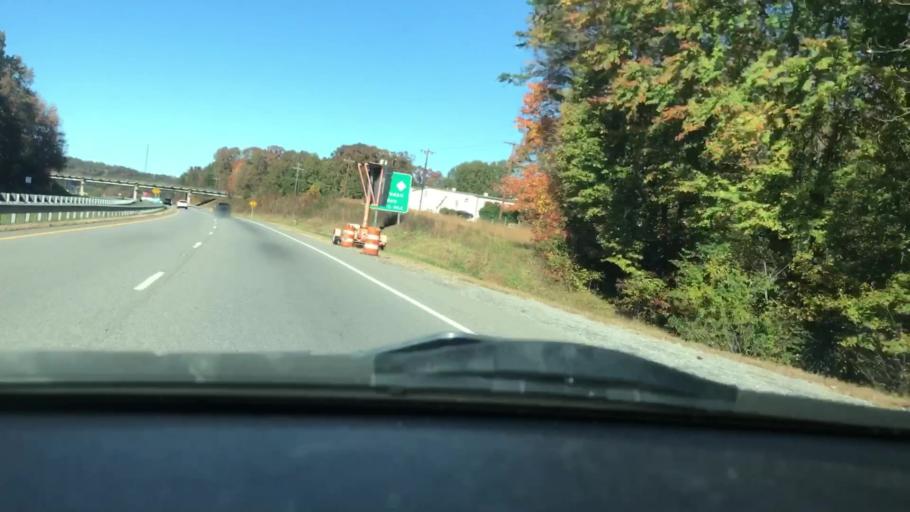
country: US
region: North Carolina
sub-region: Rockingham County
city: Madison
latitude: 36.4051
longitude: -79.9376
